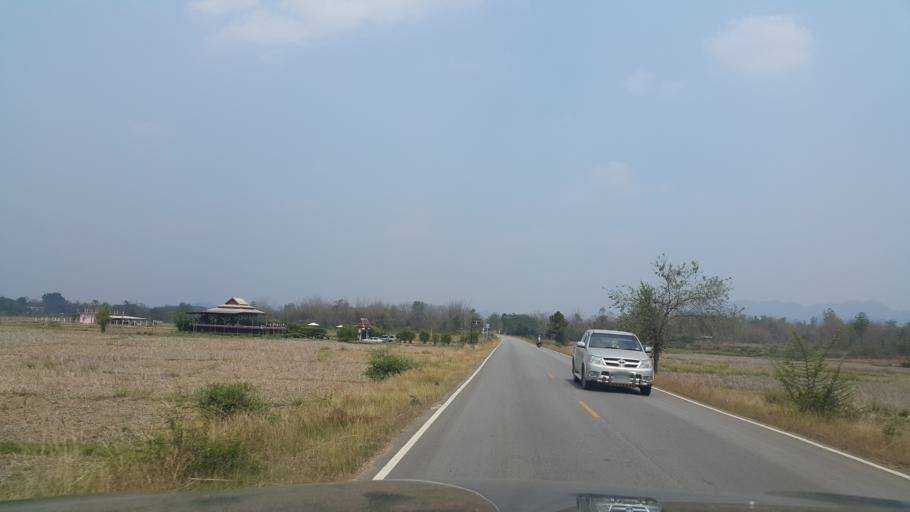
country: TH
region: Lampang
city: Soem Ngam
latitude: 18.0119
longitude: 99.2117
